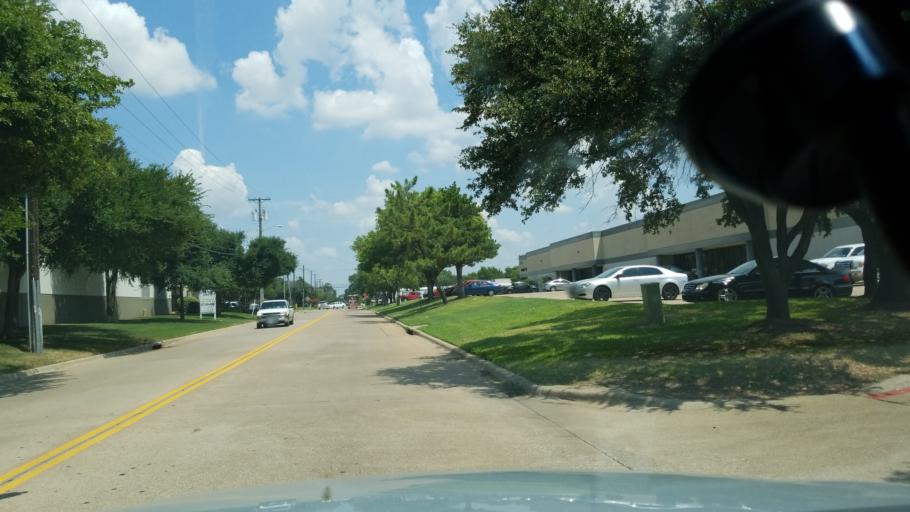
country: US
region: Texas
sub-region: Dallas County
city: Farmers Branch
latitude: 32.8649
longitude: -96.8905
